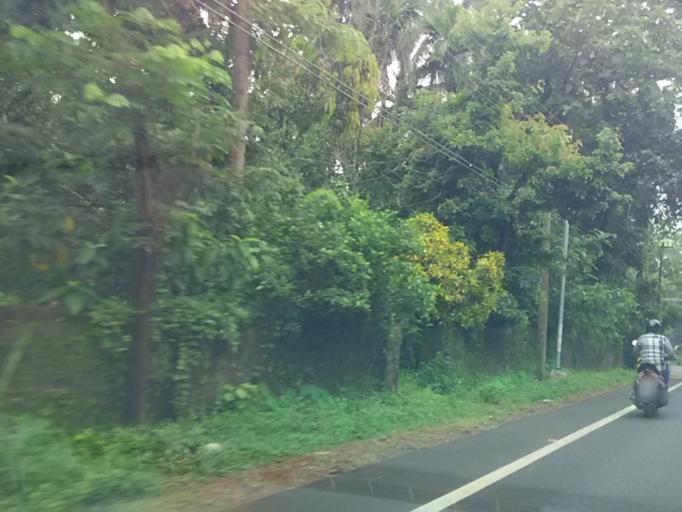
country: IN
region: Kerala
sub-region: Kozhikode
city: Kunnamangalam
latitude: 11.3005
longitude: 75.8590
